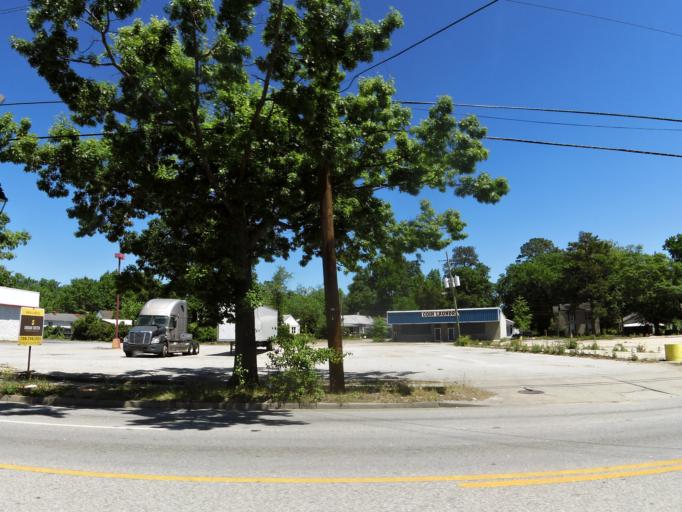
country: US
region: Georgia
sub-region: Richmond County
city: Augusta
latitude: 33.4758
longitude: -82.0030
